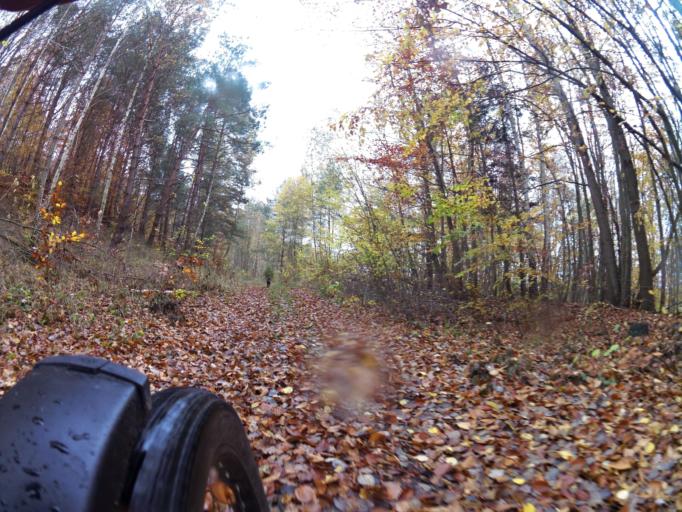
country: PL
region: Pomeranian Voivodeship
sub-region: Powiat wejherowski
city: Gniewino
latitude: 54.7546
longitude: 18.0827
